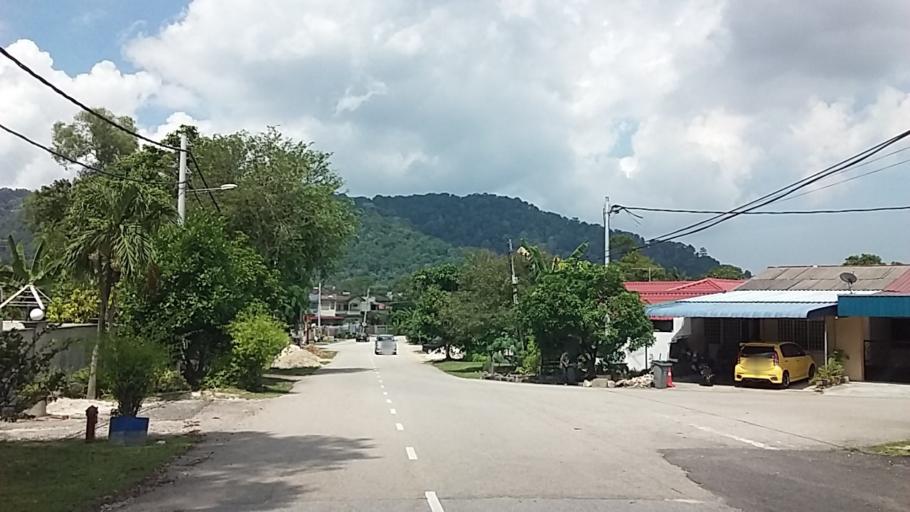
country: MY
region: Johor
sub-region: Daerah Batu Pahat
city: Batu Pahat
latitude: 1.8430
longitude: 102.9486
